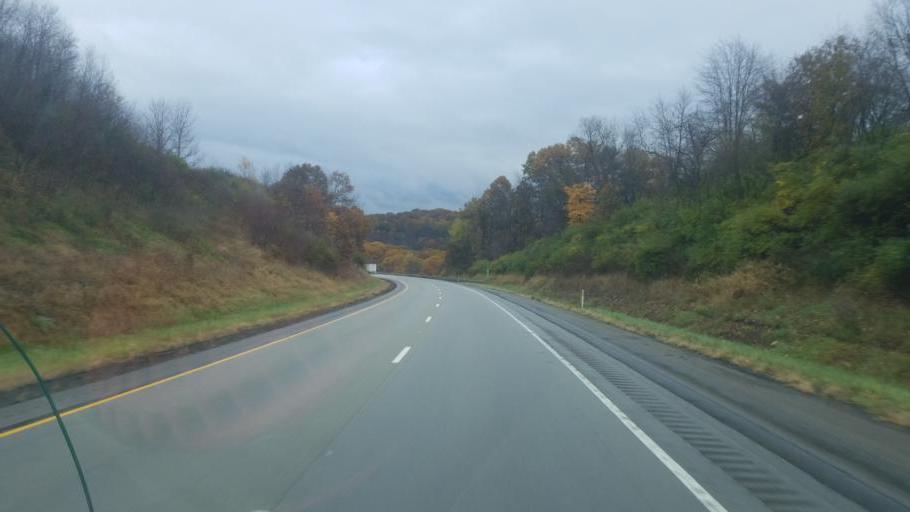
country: US
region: Pennsylvania
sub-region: Clarion County
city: Clarion
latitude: 41.1785
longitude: -79.3774
